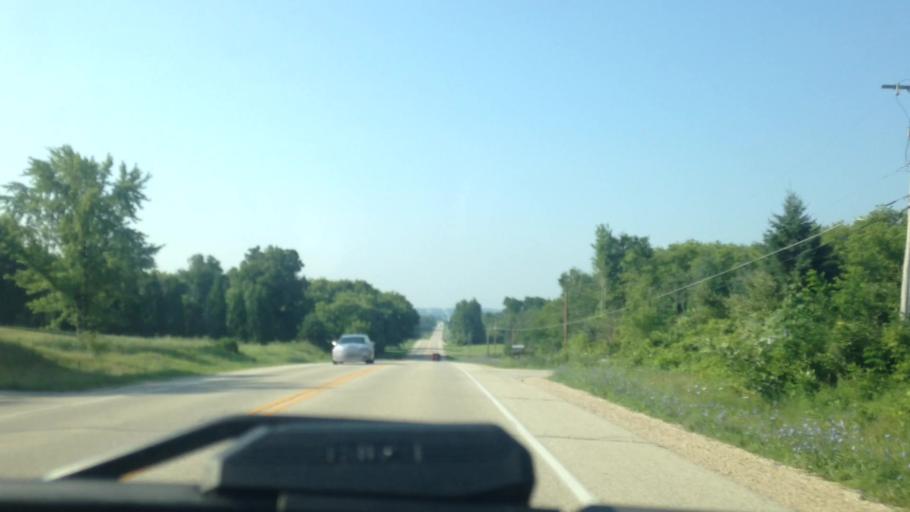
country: US
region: Wisconsin
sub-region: Washington County
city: Slinger
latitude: 43.3022
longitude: -88.2608
